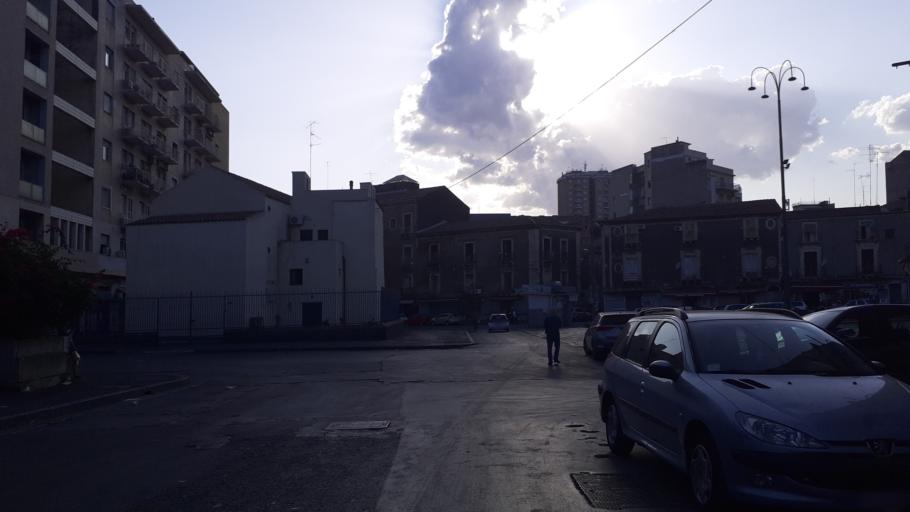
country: IT
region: Sicily
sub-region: Catania
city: Catania
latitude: 37.5089
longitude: 15.0889
